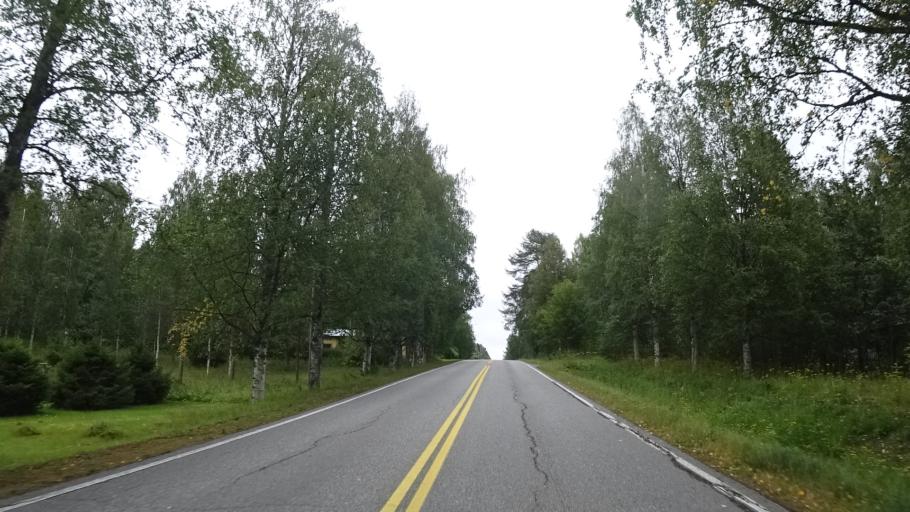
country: FI
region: North Karelia
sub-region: Pielisen Karjala
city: Lieksa
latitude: 63.2844
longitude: 30.5291
